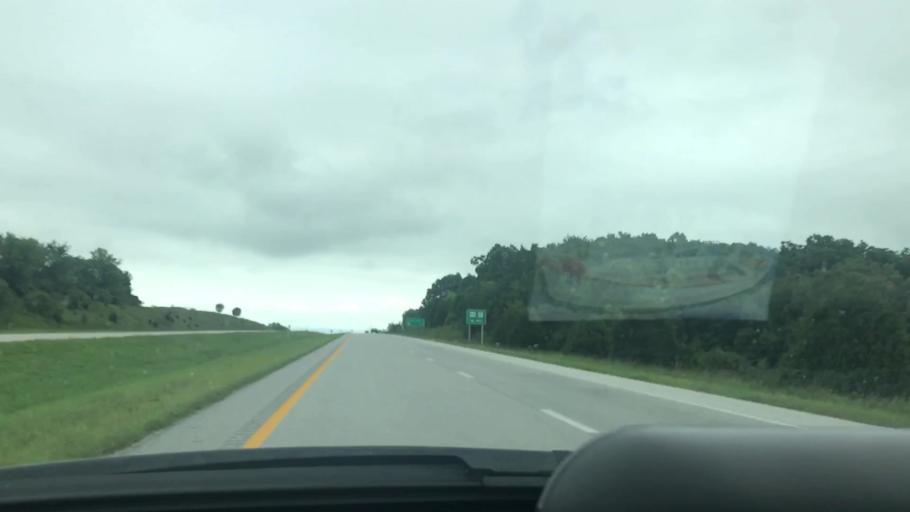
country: US
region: Missouri
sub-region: Greene County
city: Strafford
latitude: 37.2963
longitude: -93.1790
